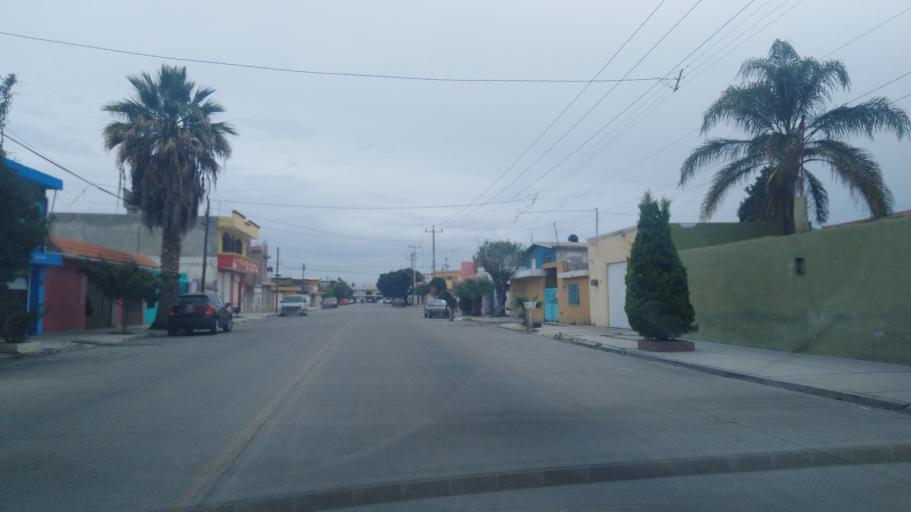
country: MX
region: Durango
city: Victoria de Durango
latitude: 24.0297
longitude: -104.6262
